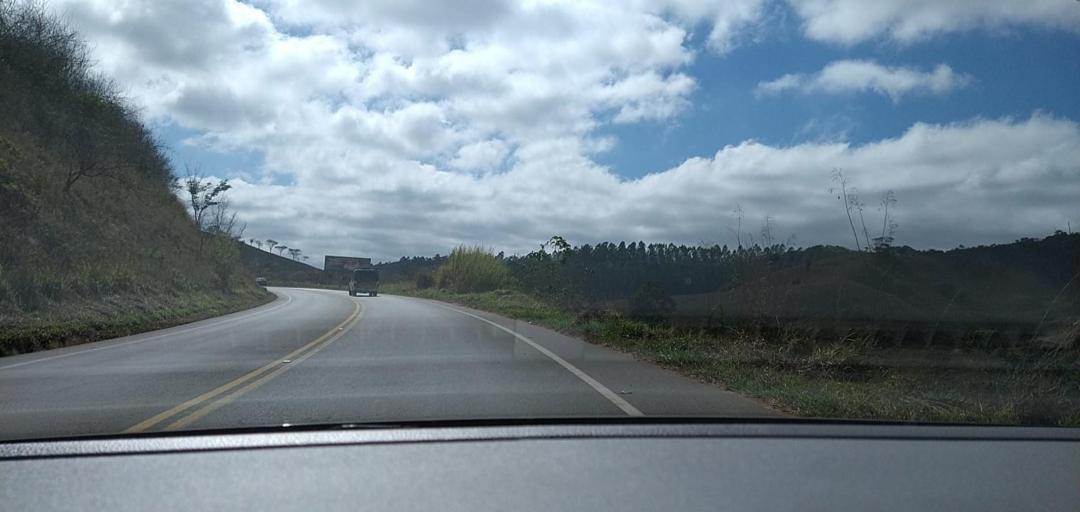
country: BR
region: Minas Gerais
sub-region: Vicosa
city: Vicosa
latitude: -20.7037
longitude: -42.8611
